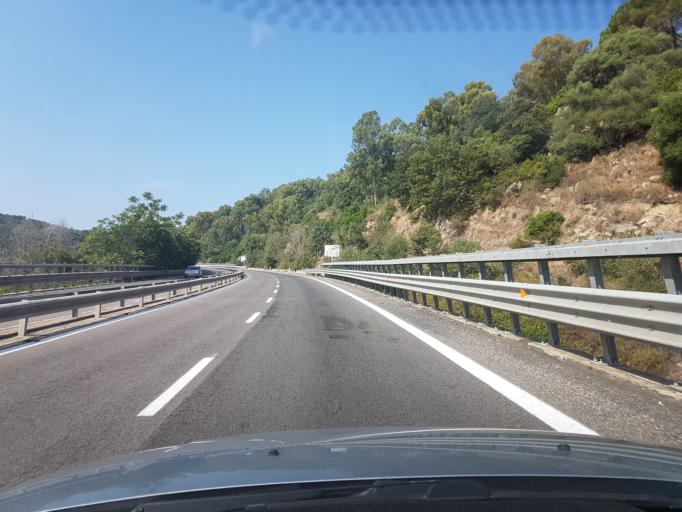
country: IT
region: Sardinia
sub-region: Provincia di Nuoro
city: Nuoro
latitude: 40.3391
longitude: 9.3028
